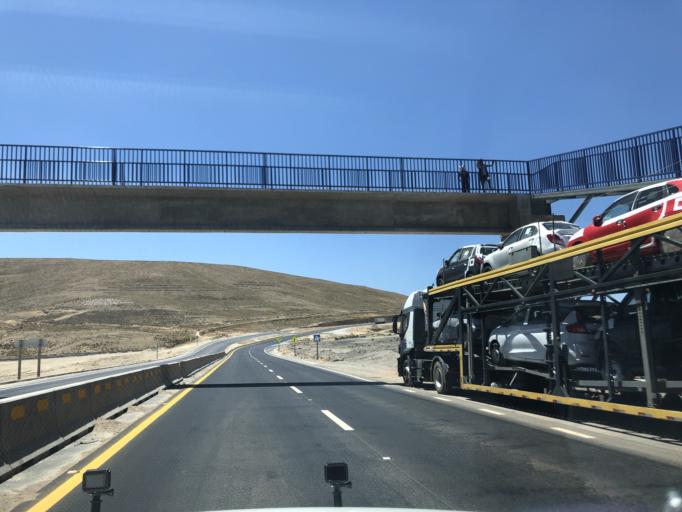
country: BO
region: Cochabamba
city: Colchani
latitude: -17.6948
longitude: -66.7624
